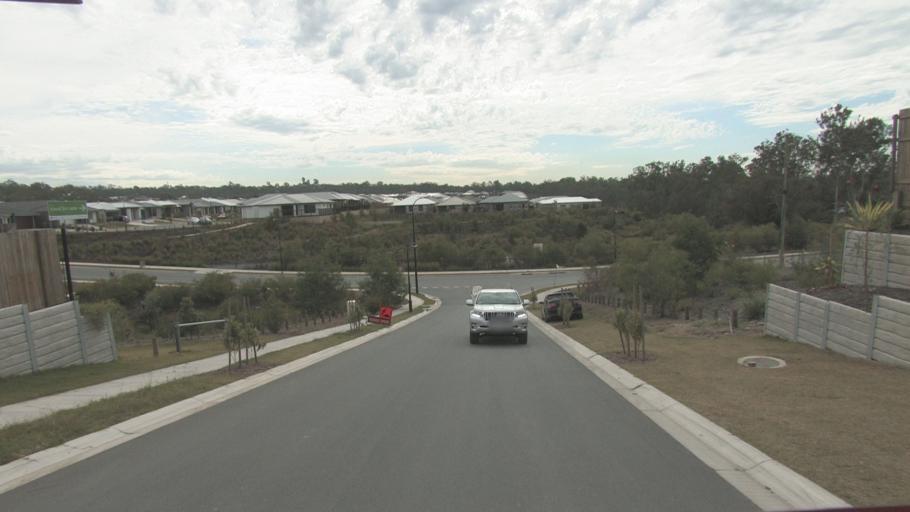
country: AU
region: Queensland
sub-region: Logan
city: Windaroo
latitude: -27.7227
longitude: 153.1651
